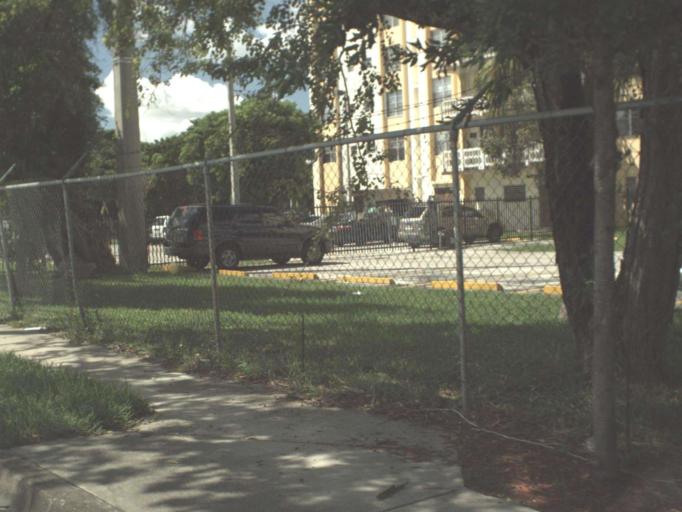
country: US
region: Florida
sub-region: Miami-Dade County
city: Golden Glades
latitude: 25.9181
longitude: -80.2121
